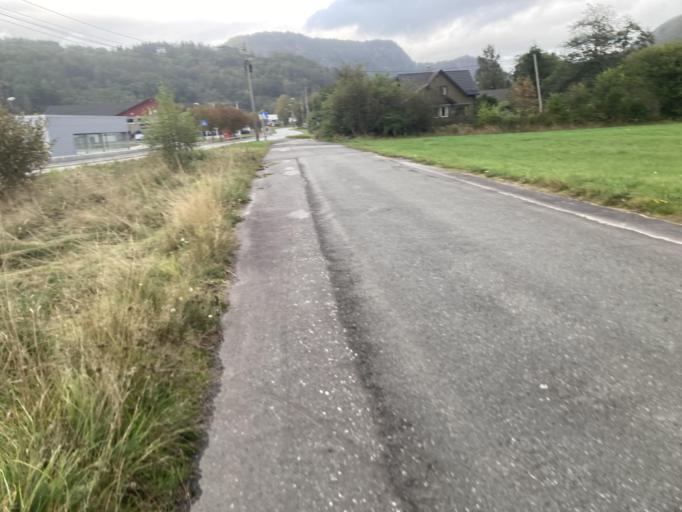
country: NO
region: Vest-Agder
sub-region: Kvinesdal
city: Liknes
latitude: 58.3204
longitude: 6.9651
